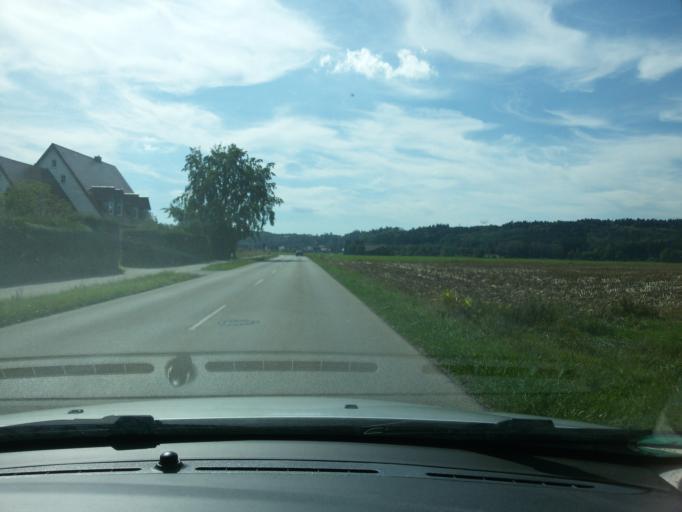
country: DE
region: Bavaria
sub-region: Swabia
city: Bobingen
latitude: 48.2805
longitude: 10.8104
